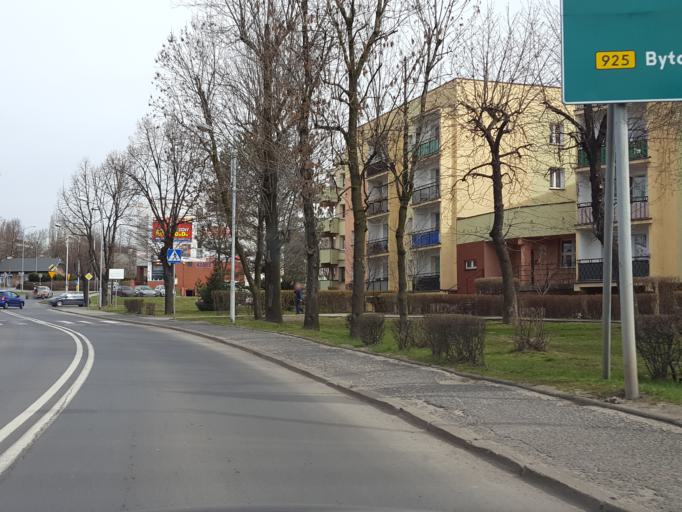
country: PL
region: Silesian Voivodeship
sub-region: Ruda Slaska
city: Ruda Slaska
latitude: 50.2692
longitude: 18.8729
